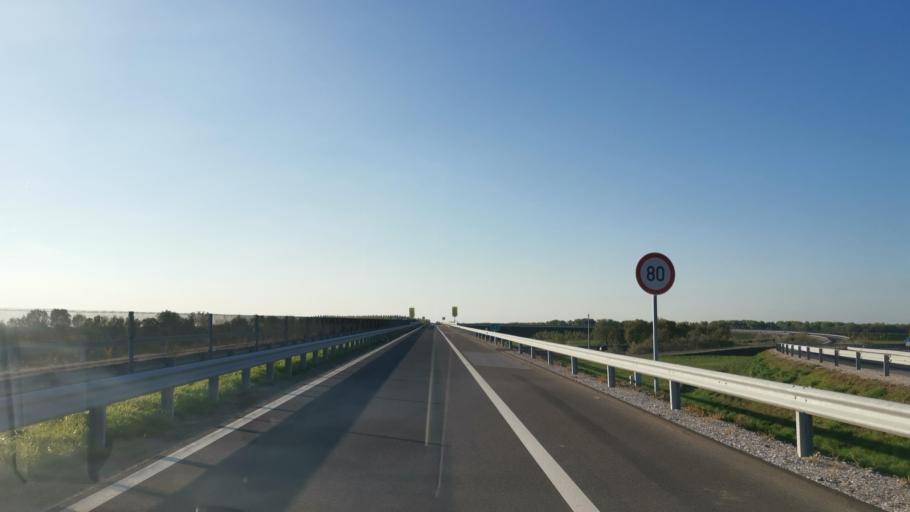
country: HU
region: Heves
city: Erdotelek
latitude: 47.7279
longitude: 20.3417
